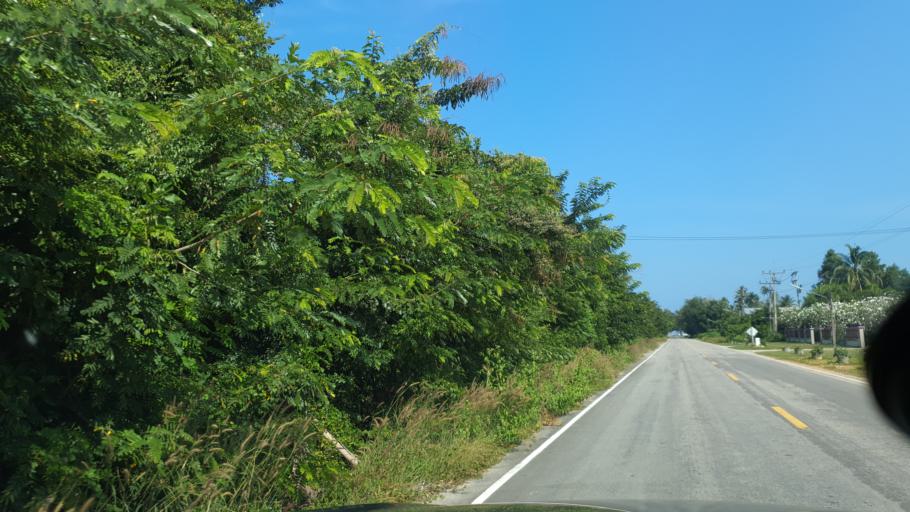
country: TH
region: Surat Thani
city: Tha Chana
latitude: 9.5874
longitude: 99.2031
